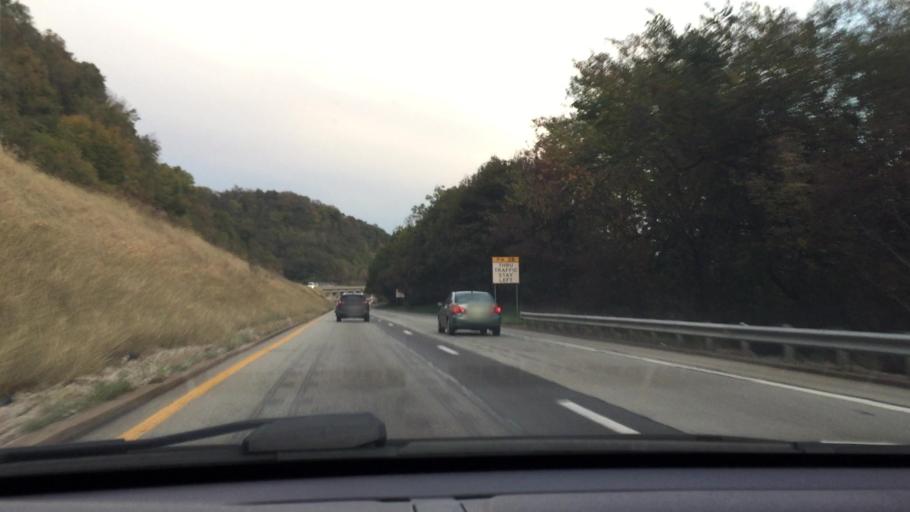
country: US
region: Pennsylvania
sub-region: Allegheny County
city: Sharpsburg
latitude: 40.4973
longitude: -79.9305
